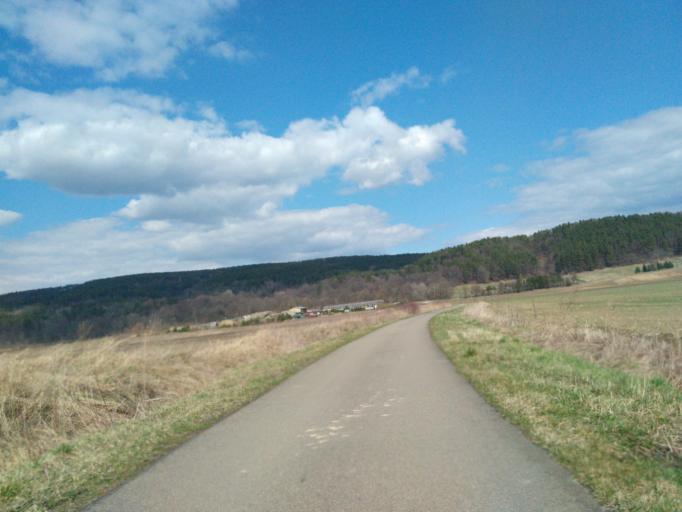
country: PL
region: Subcarpathian Voivodeship
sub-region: Powiat brzozowski
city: Dydnia
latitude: 49.6718
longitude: 22.2646
